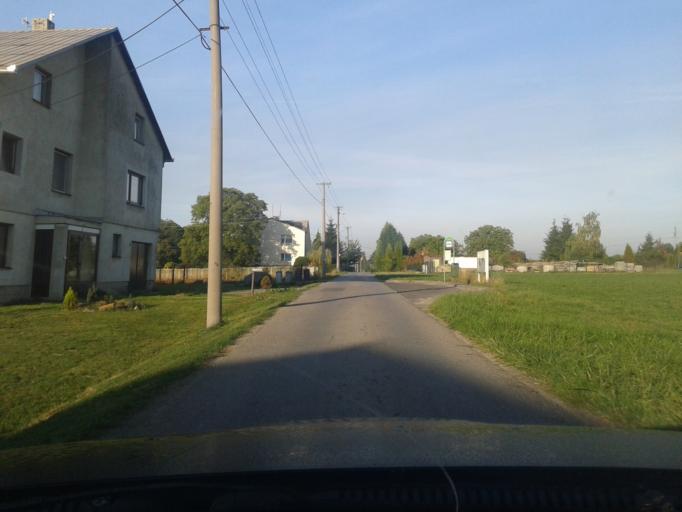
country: CZ
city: Dolni Lutyne
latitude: 49.8821
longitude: 18.4111
